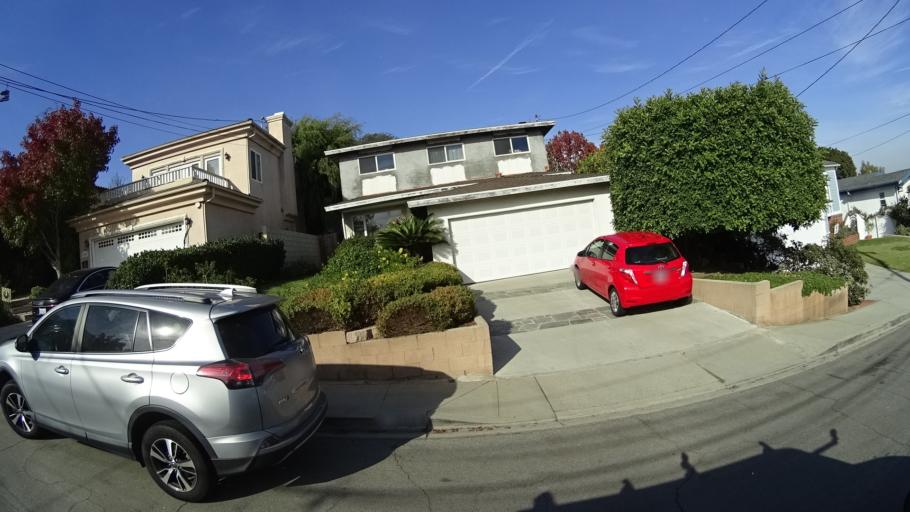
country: US
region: California
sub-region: Los Angeles County
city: Hermosa Beach
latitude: 33.8738
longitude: -118.3825
